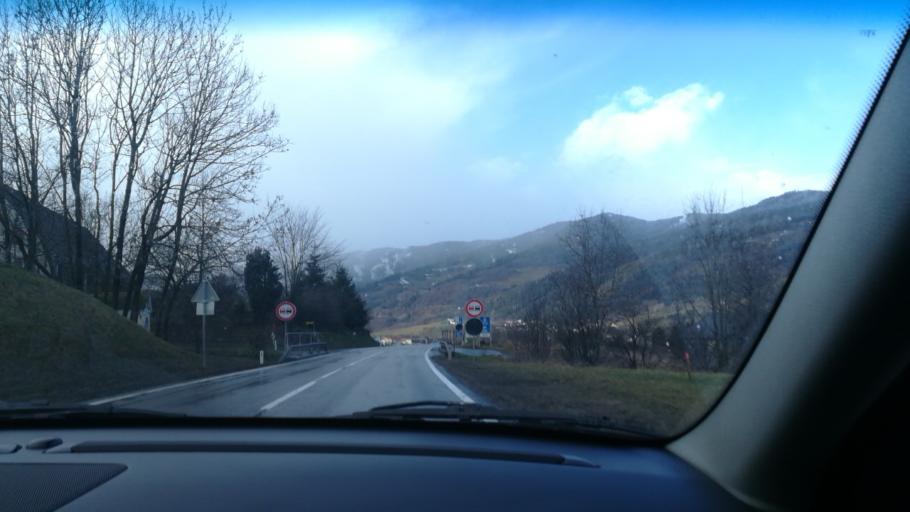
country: AT
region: Styria
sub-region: Politischer Bezirk Murtal
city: Sankt Georgen ob Judenburg
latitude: 47.2026
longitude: 14.5122
